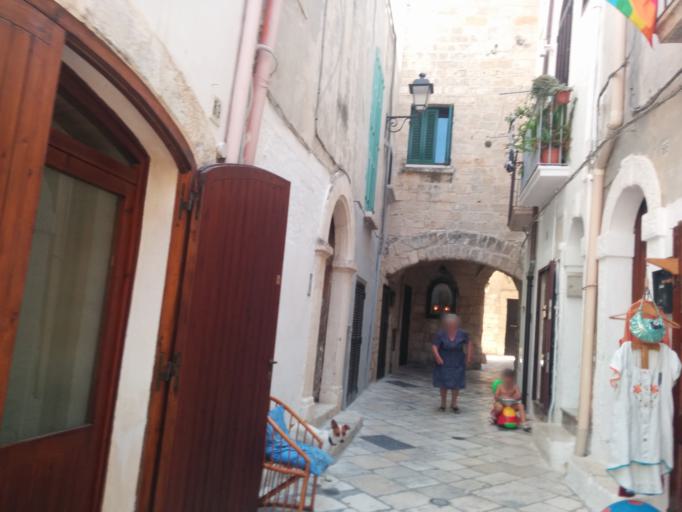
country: IT
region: Apulia
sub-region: Provincia di Bari
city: Polignano a Mare
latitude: 40.9970
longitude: 17.2191
